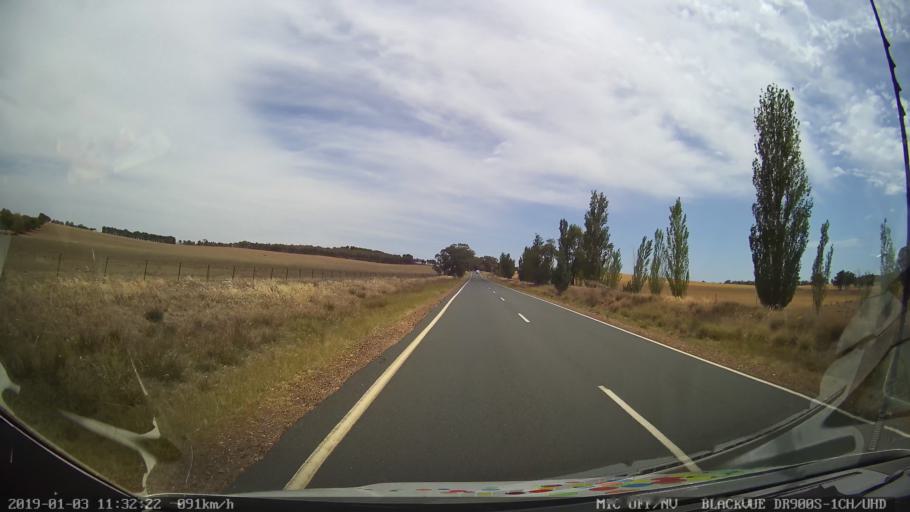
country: AU
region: New South Wales
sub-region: Weddin
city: Grenfell
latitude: -33.9593
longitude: 148.1790
